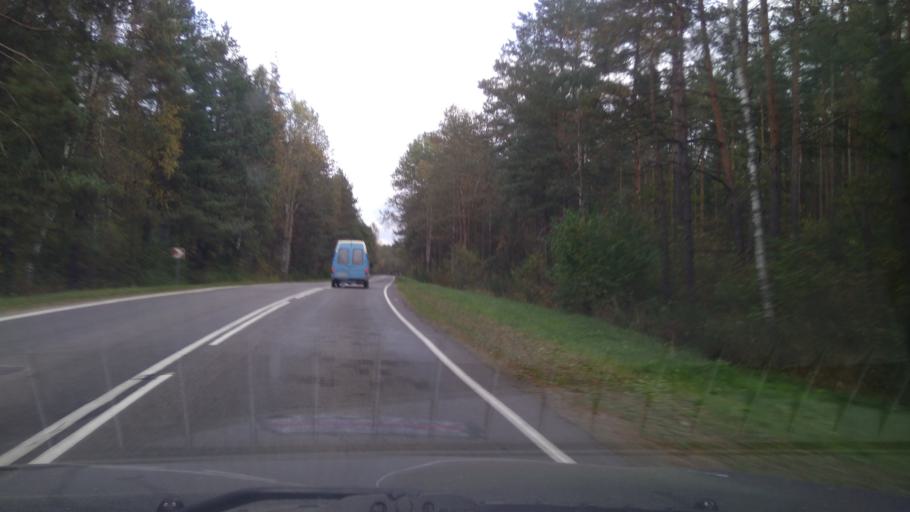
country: BY
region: Minsk
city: Druzhny
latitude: 53.6388
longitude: 27.9016
